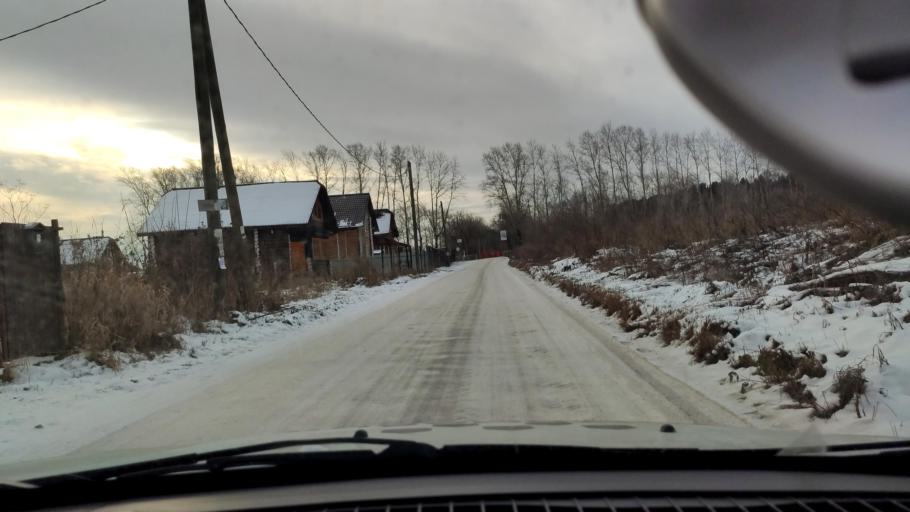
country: RU
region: Perm
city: Lobanovo
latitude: 57.8273
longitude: 56.3545
